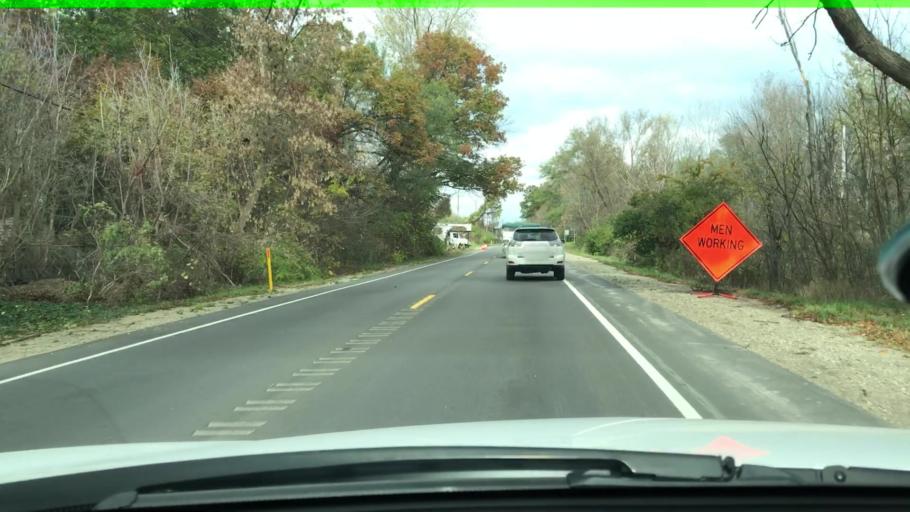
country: US
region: Michigan
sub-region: Oakland County
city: Waterford
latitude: 42.6501
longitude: -83.4435
